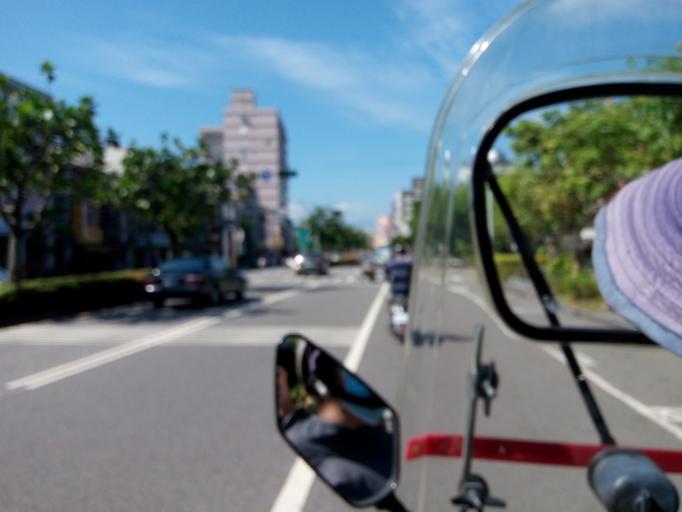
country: TW
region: Taiwan
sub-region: Yilan
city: Yilan
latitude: 24.6805
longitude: 121.7624
